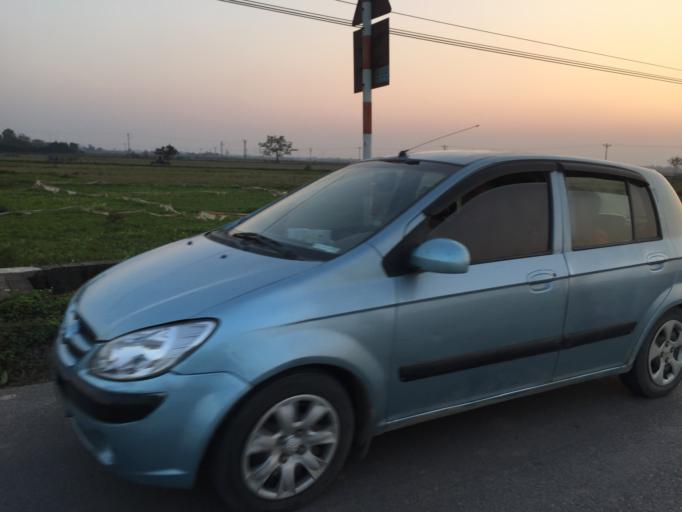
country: VN
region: Ha Noi
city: Chuc Son
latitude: 20.8918
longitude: 105.7196
